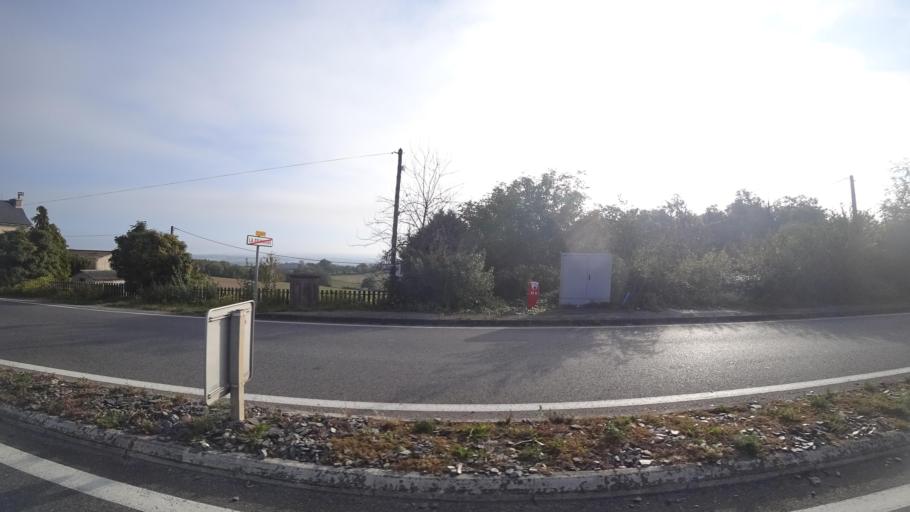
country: FR
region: Midi-Pyrenees
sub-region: Departement de l'Aveyron
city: Luc-la-Primaube
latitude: 44.3014
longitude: 2.5568
